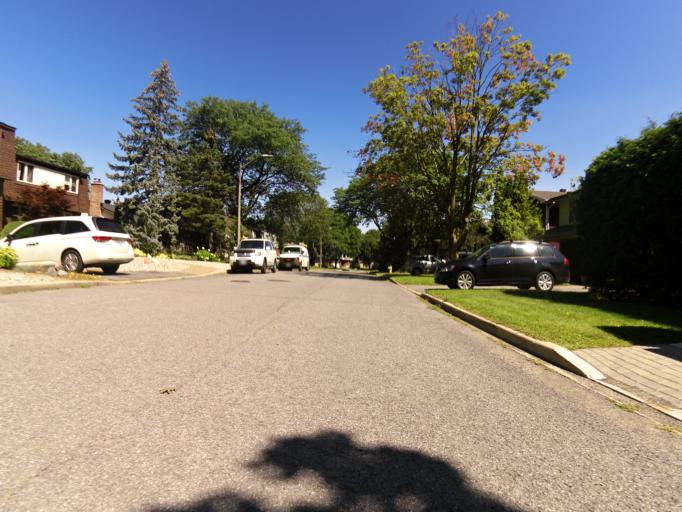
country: CA
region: Ontario
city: Ottawa
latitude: 45.3548
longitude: -75.6695
